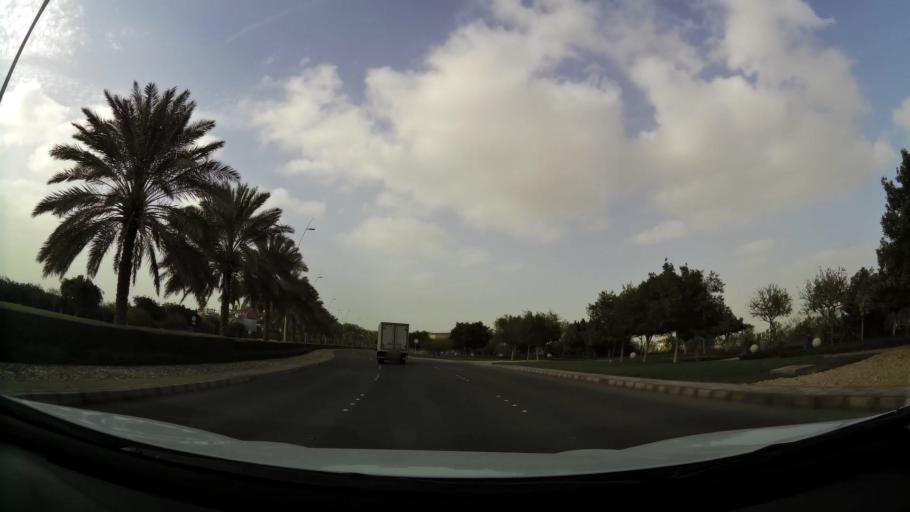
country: AE
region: Abu Dhabi
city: Abu Dhabi
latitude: 24.4847
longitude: 54.6028
